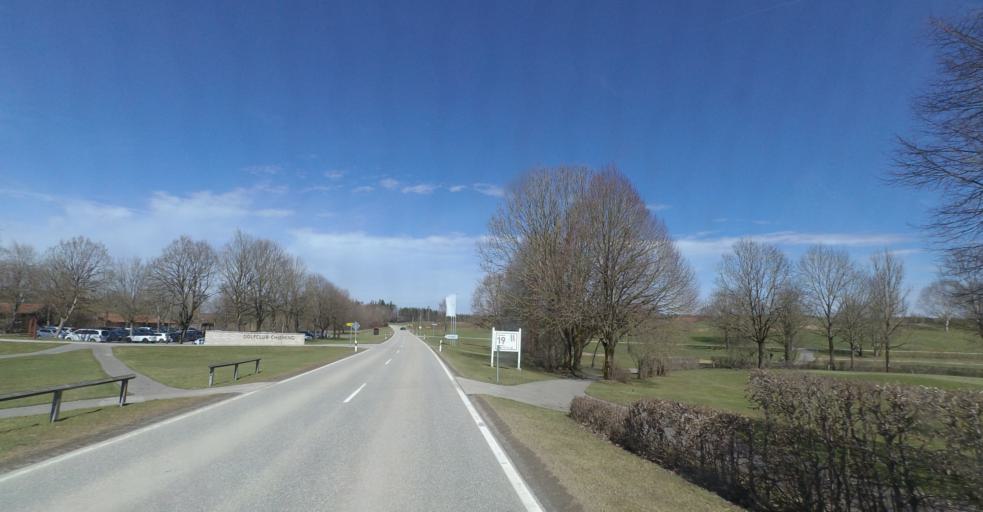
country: DE
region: Bavaria
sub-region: Upper Bavaria
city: Chieming
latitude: 47.9355
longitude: 12.5537
